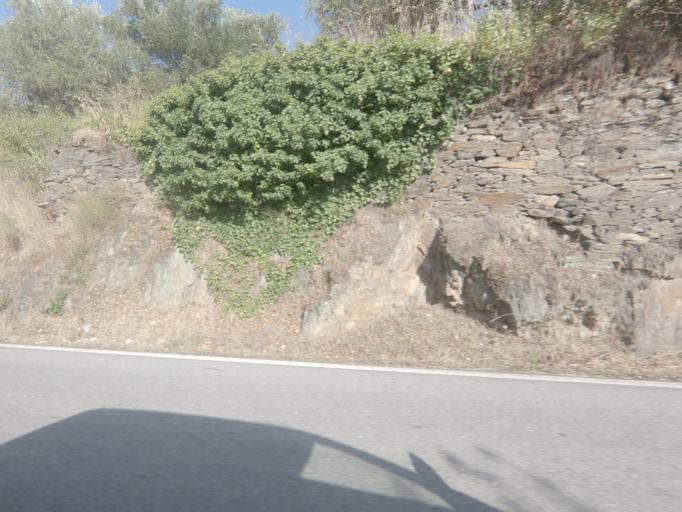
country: PT
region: Viseu
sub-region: Tabuaco
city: Tabuaco
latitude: 41.1731
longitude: -7.5539
